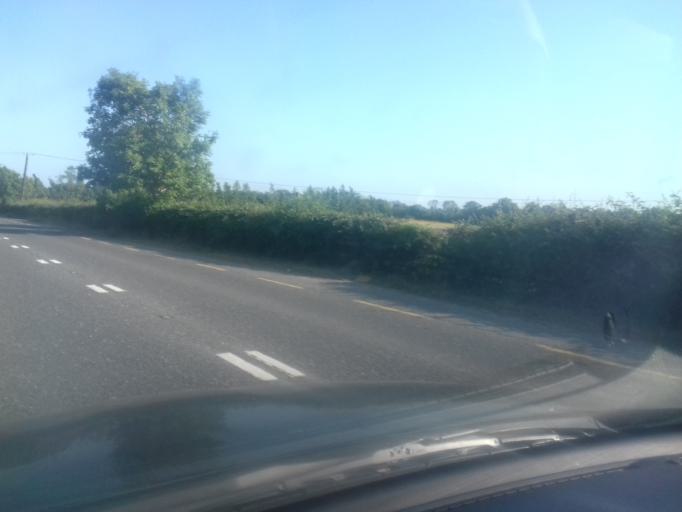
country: IE
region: Leinster
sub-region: An Mhi
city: Ashbourne
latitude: 53.4916
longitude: -6.3799
